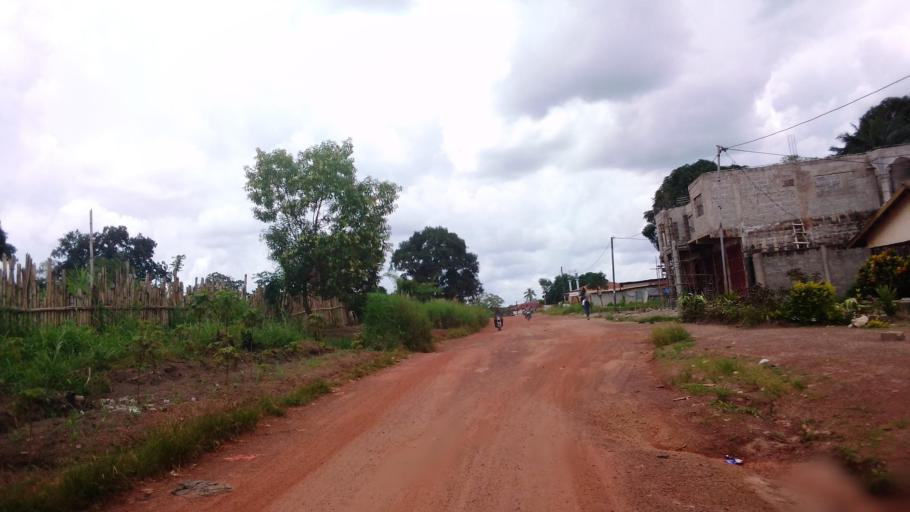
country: SL
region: Northern Province
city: Makeni
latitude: 8.8700
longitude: -12.0331
